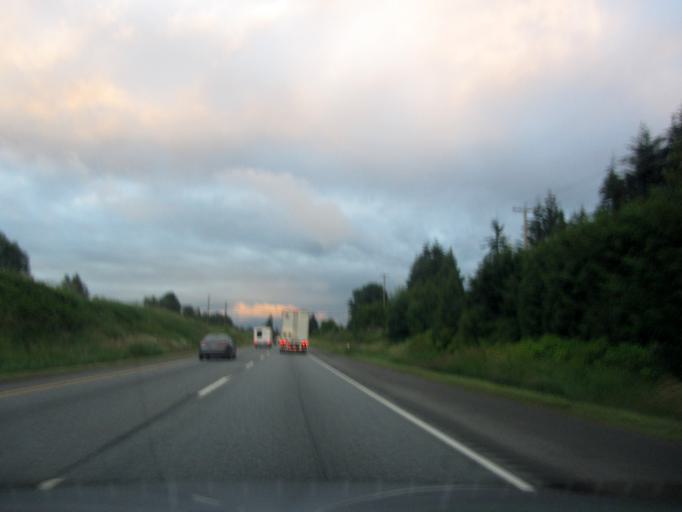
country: CA
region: British Columbia
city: Aldergrove
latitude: 49.0933
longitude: -122.4725
